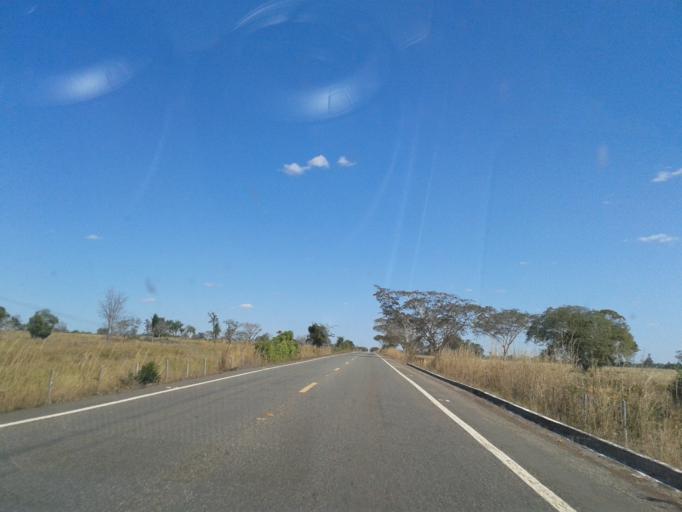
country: BR
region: Goias
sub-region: Sao Miguel Do Araguaia
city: Sao Miguel do Araguaia
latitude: -13.6398
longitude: -50.3154
